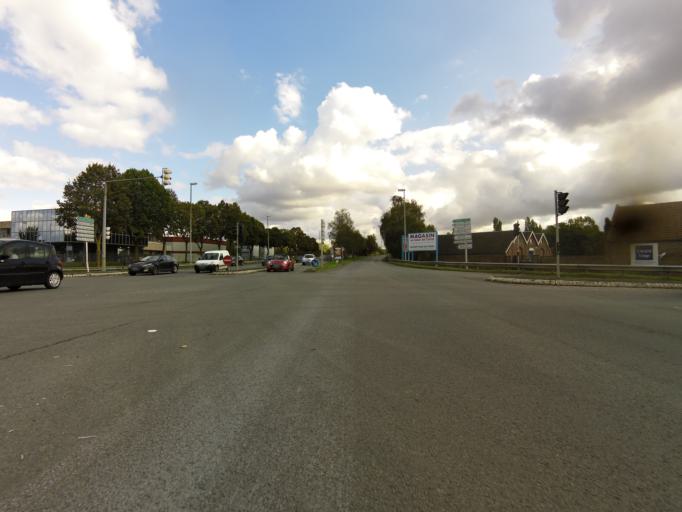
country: FR
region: Nord-Pas-de-Calais
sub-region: Departement du Nord
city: Neuville-Saint-Remy
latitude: 50.1747
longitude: 3.2161
